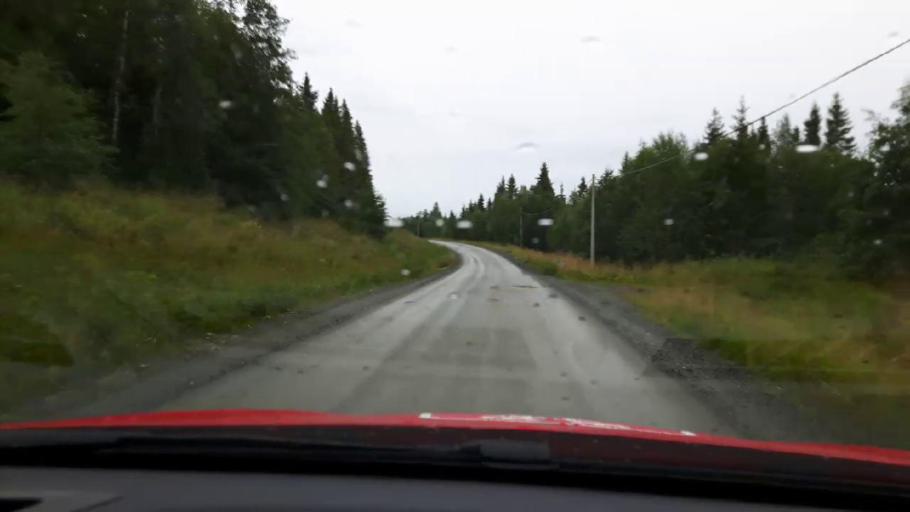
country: SE
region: Jaemtland
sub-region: Are Kommun
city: Are
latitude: 63.4906
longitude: 12.7689
